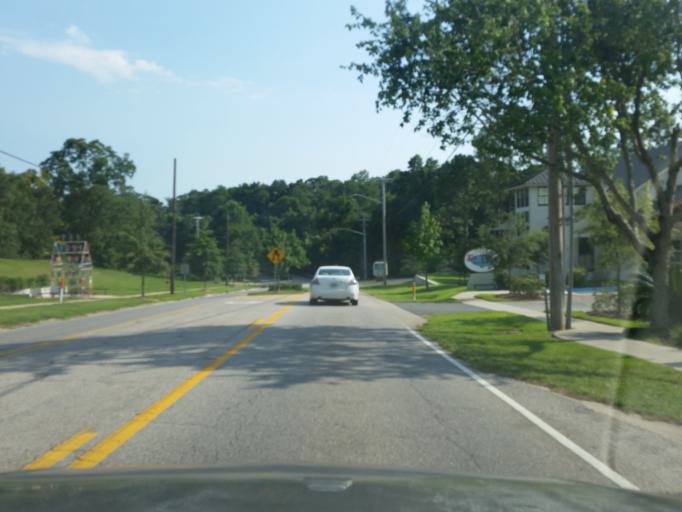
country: US
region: Alabama
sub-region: Baldwin County
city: Fairhope
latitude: 30.5311
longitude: -87.9024
